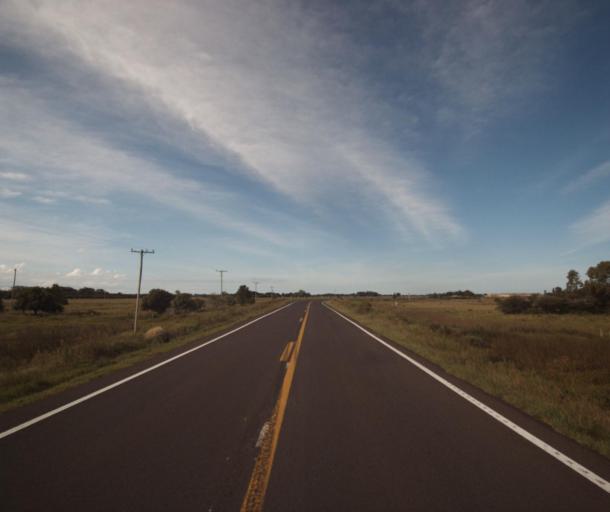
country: BR
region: Rio Grande do Sul
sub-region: Tapes
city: Tapes
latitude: -31.3171
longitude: -51.1204
